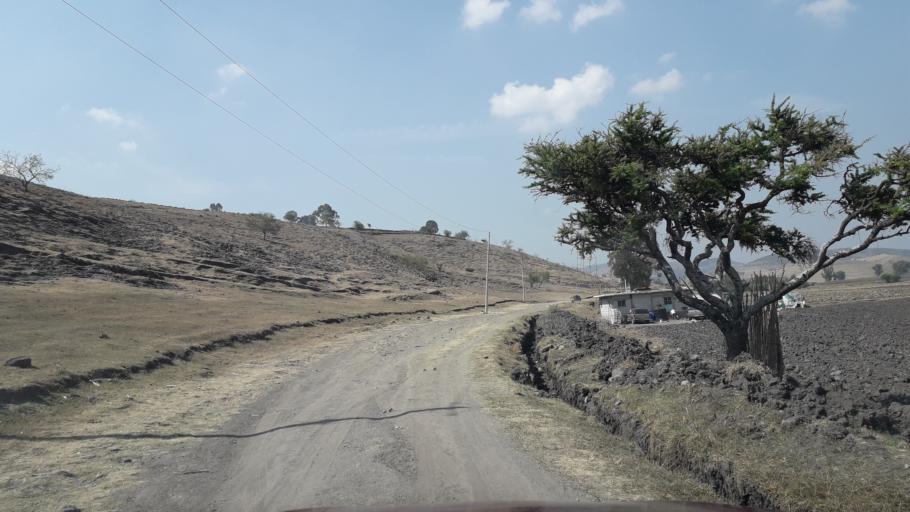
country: MX
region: Puebla
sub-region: Puebla
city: San Andres Azumiatla
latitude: 18.9229
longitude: -98.2559
